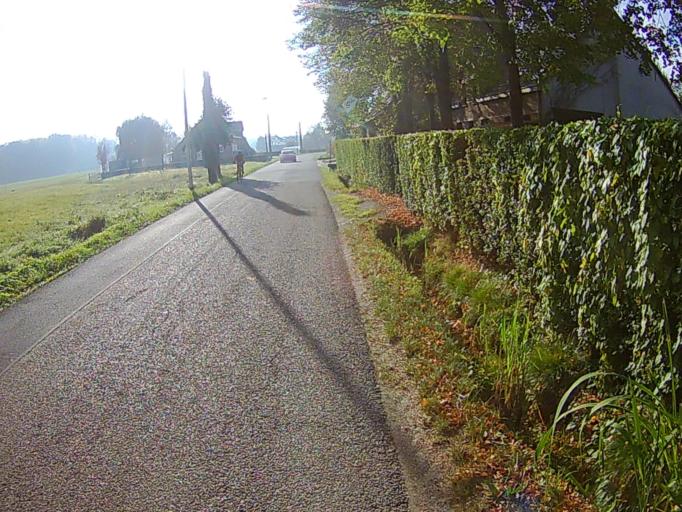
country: BE
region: Flanders
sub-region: Provincie Antwerpen
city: Lint
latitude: 51.1411
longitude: 4.5130
